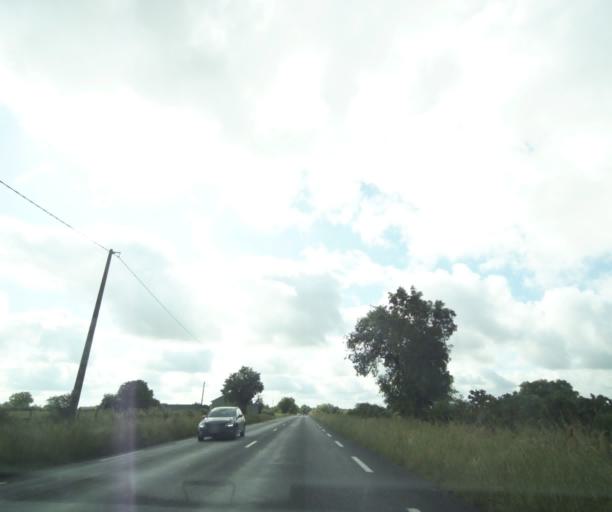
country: FR
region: Pays de la Loire
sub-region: Departement de la Sarthe
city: Vion
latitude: 47.7971
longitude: -0.2602
